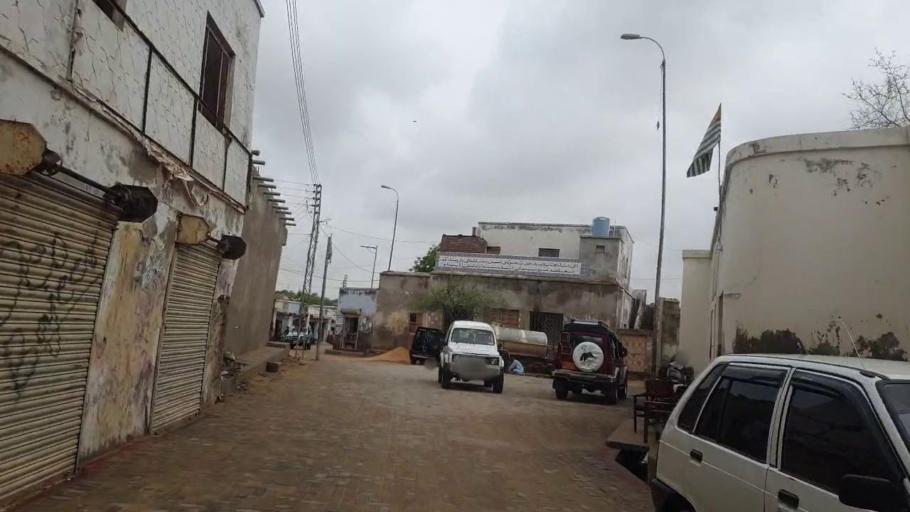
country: PK
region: Sindh
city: Diplo
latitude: 24.4681
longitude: 69.5809
